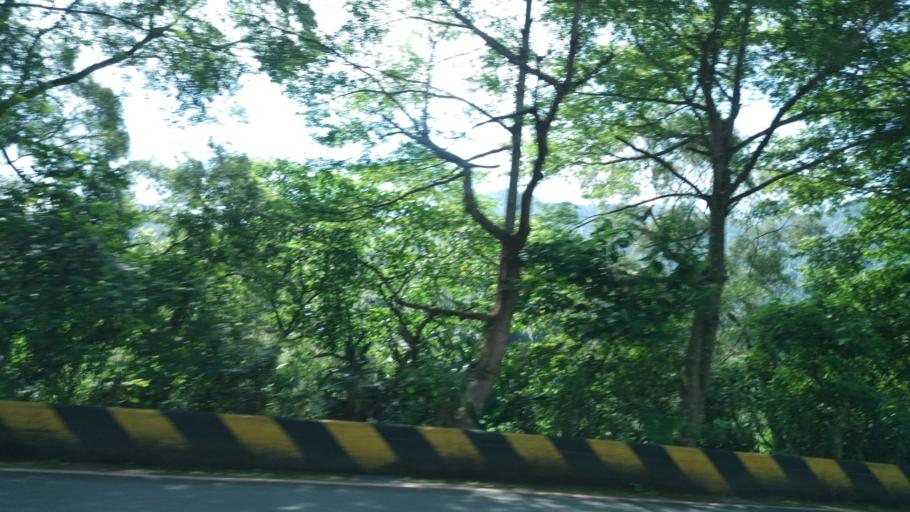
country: TW
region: Taipei
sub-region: Taipei
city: Banqiao
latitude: 24.9456
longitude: 121.5043
